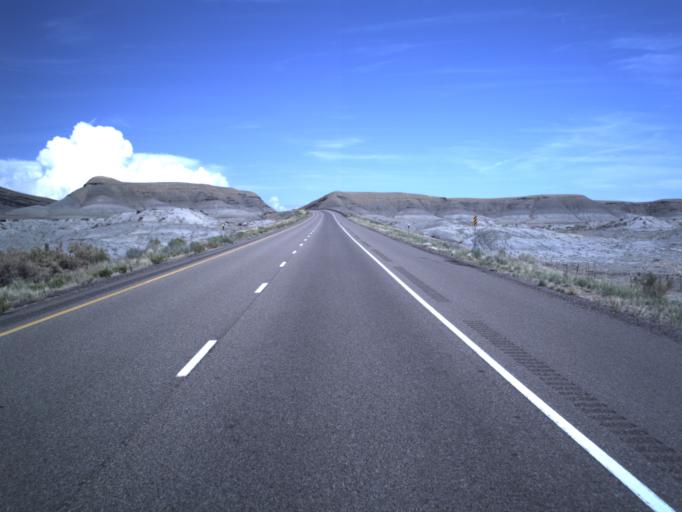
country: US
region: Utah
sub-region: Carbon County
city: East Carbon City
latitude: 38.9358
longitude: -110.3453
